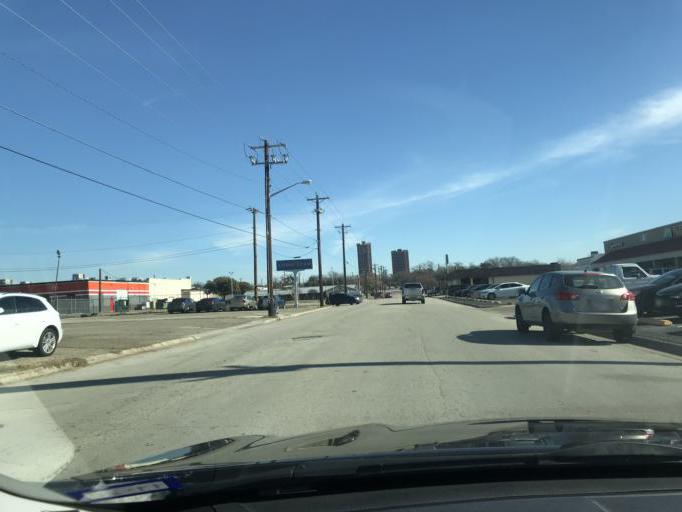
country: US
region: Texas
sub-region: Denton County
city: Denton
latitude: 33.2296
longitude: -97.1389
